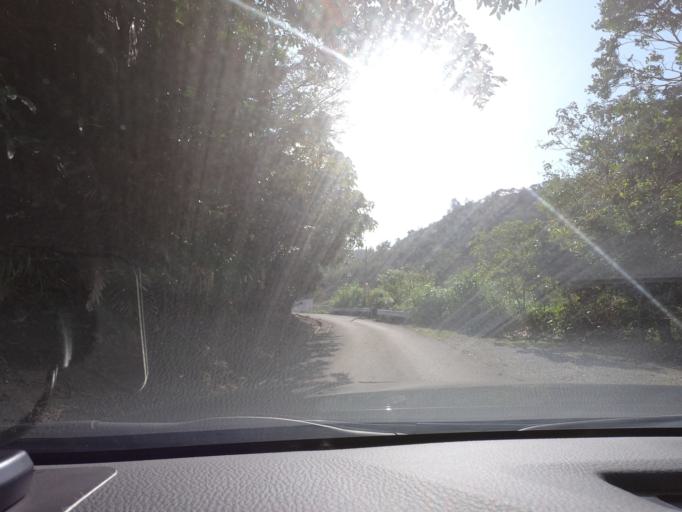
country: JP
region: Okinawa
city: Nago
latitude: 26.7572
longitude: 128.1925
